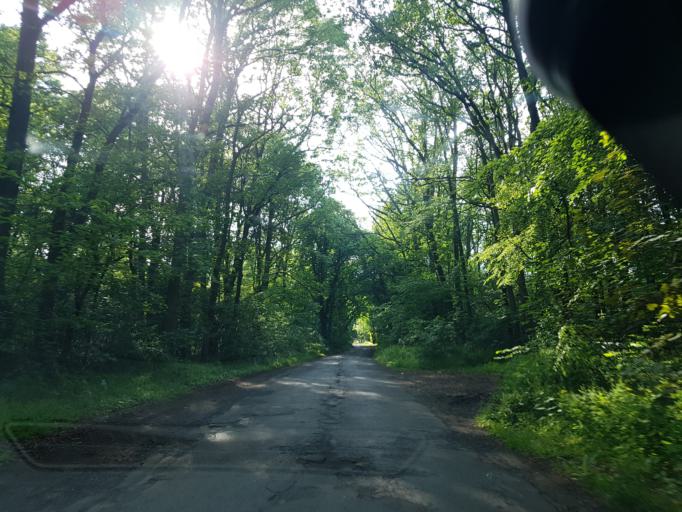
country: PL
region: Lower Silesian Voivodeship
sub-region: Powiat strzelinski
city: Wiazow
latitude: 50.8459
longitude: 17.2470
